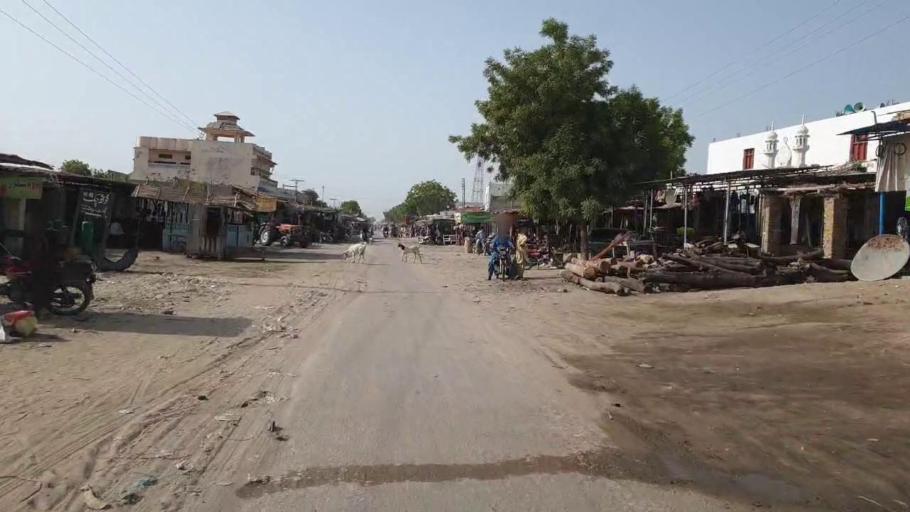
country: PK
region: Sindh
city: Sanghar
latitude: 26.2701
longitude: 68.9297
